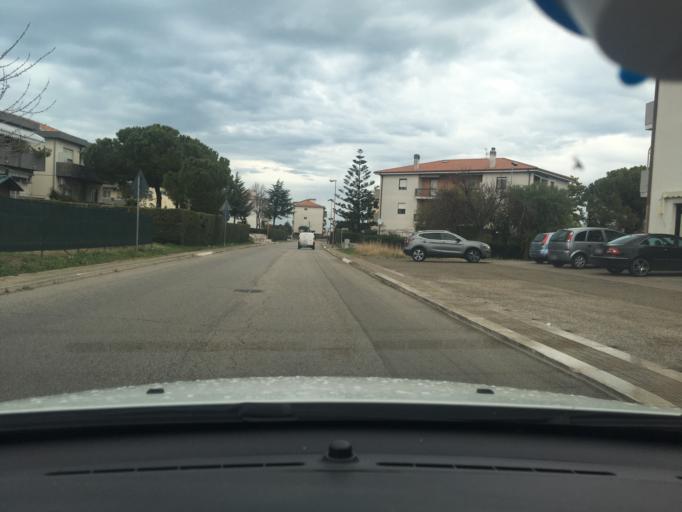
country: IT
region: Molise
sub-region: Provincia di Campobasso
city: Termoli
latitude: 41.9732
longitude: 14.9941
